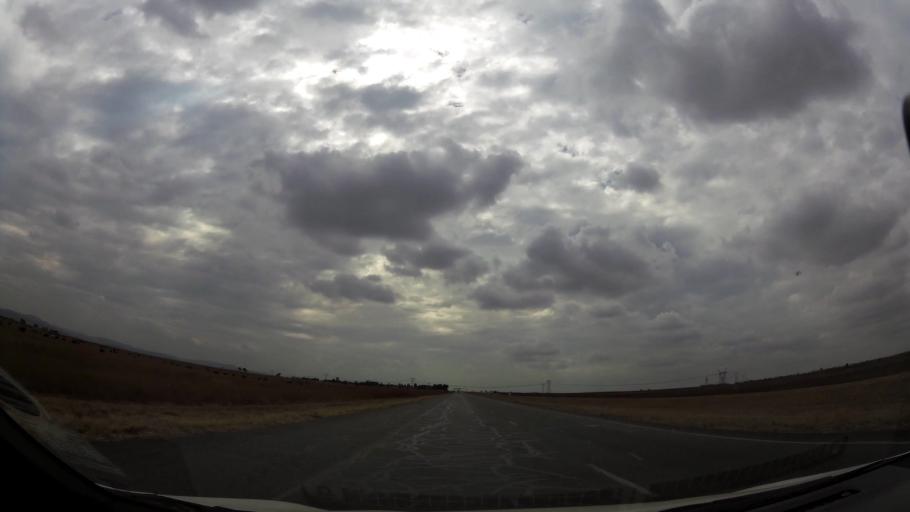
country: ZA
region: Gauteng
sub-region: Ekurhuleni Metropolitan Municipality
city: Germiston
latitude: -26.3664
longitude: 28.0935
